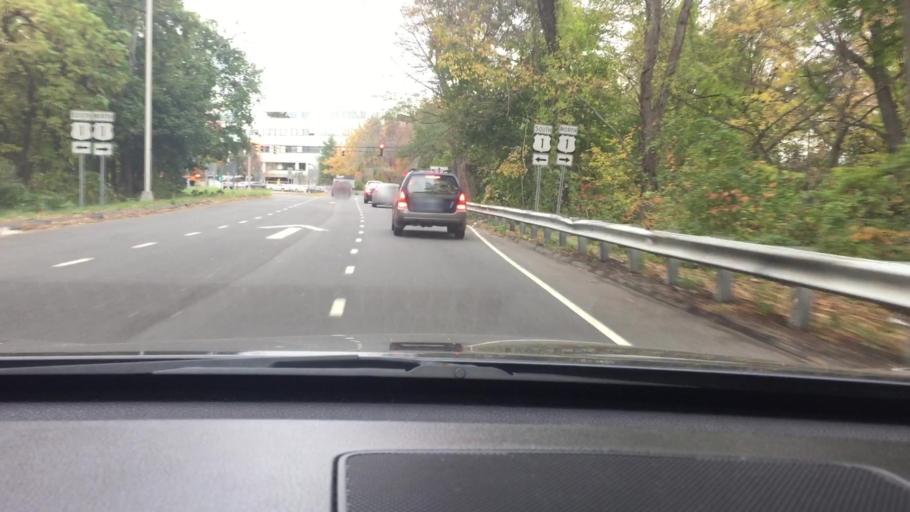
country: US
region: Connecticut
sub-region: Fairfield County
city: Darien
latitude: 41.0906
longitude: -73.4539
